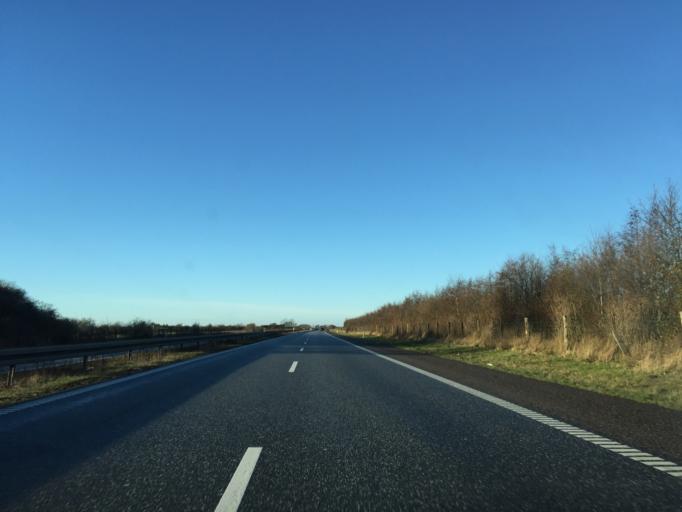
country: DK
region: South Denmark
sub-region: Nyborg Kommune
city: Nyborg
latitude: 55.3336
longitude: 10.7227
